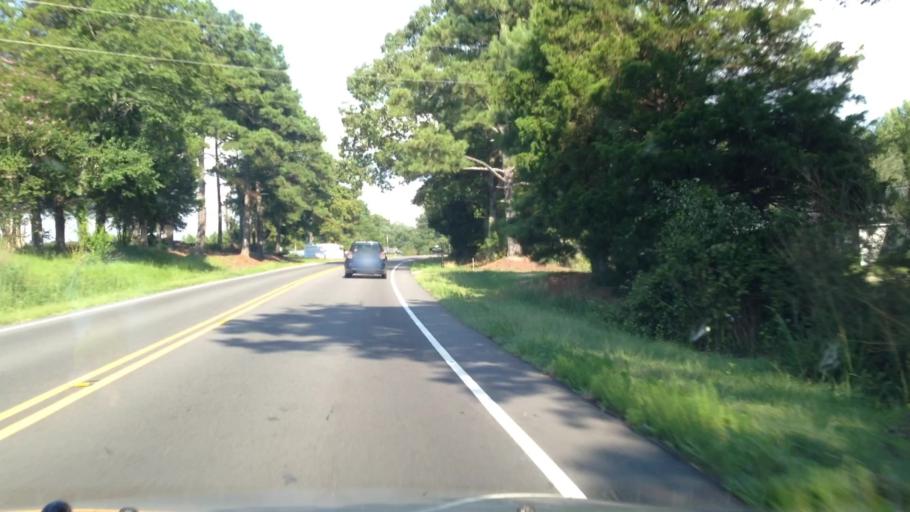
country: US
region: North Carolina
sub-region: Harnett County
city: Coats
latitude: 35.4148
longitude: -78.6997
